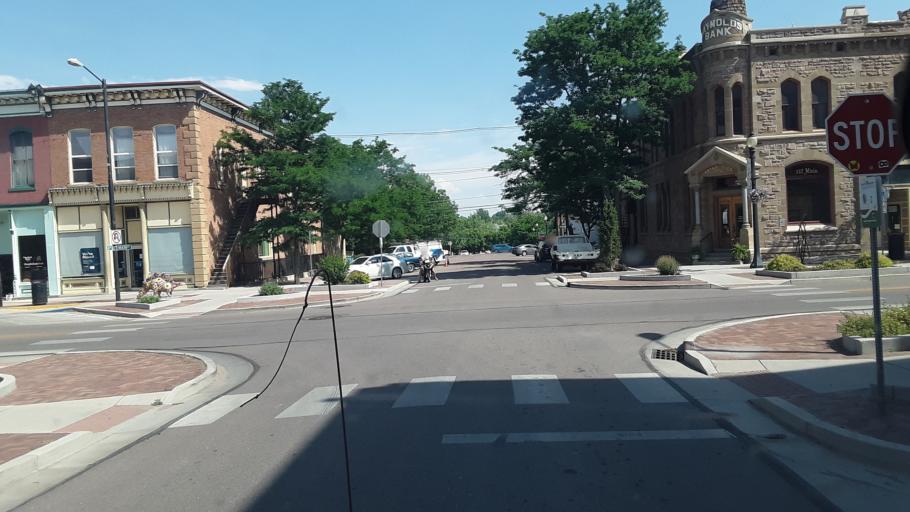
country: US
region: Colorado
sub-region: Fremont County
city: Canon City
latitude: 38.4401
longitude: -105.2422
